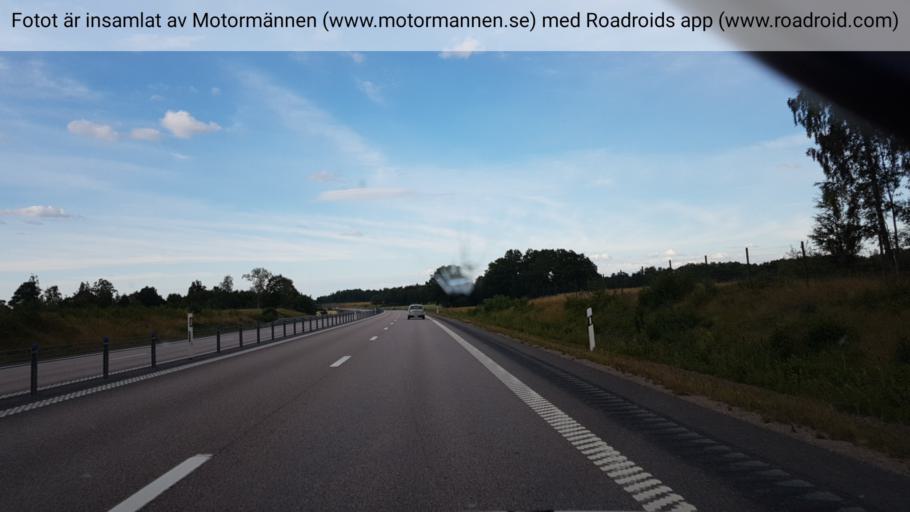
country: SE
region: Vaestra Goetaland
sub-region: Gotene Kommun
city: Goetene
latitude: 58.4947
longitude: 13.4974
